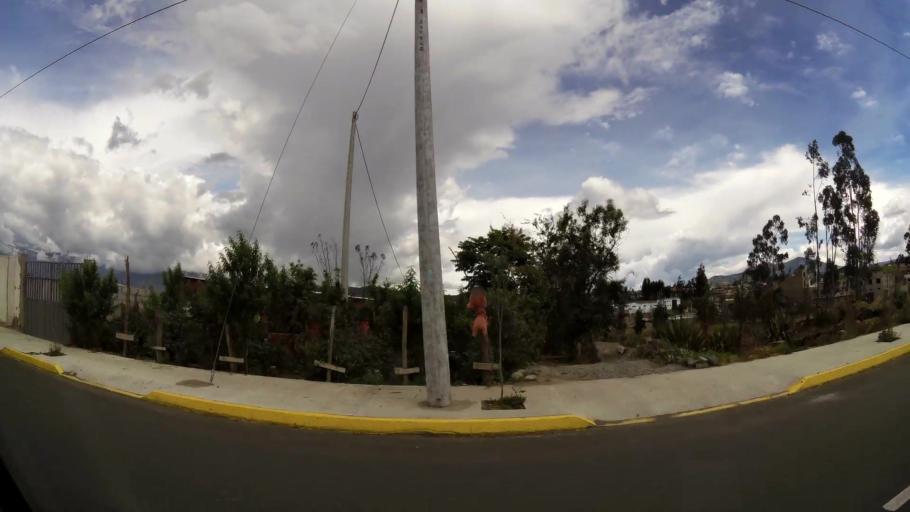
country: EC
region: Tungurahua
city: Ambato
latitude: -1.2645
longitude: -78.6080
